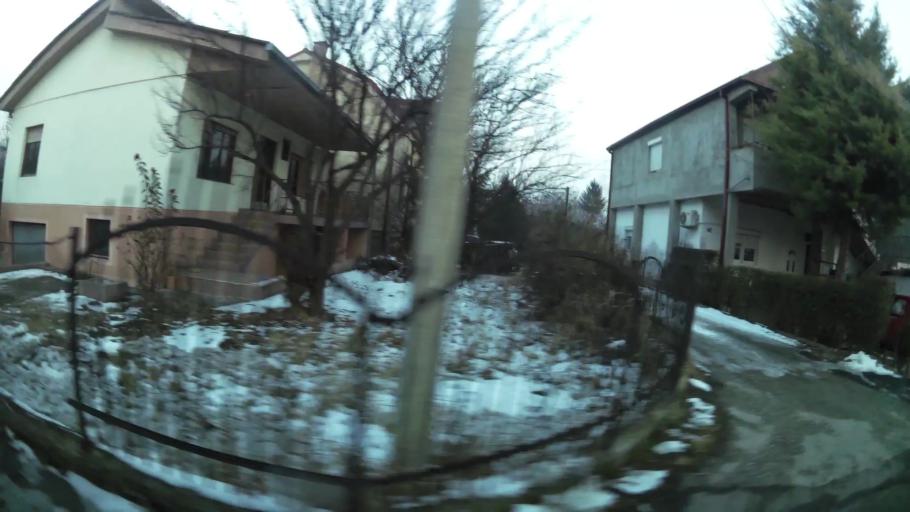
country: MK
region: Kisela Voda
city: Kisela Voda
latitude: 41.9995
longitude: 21.5065
